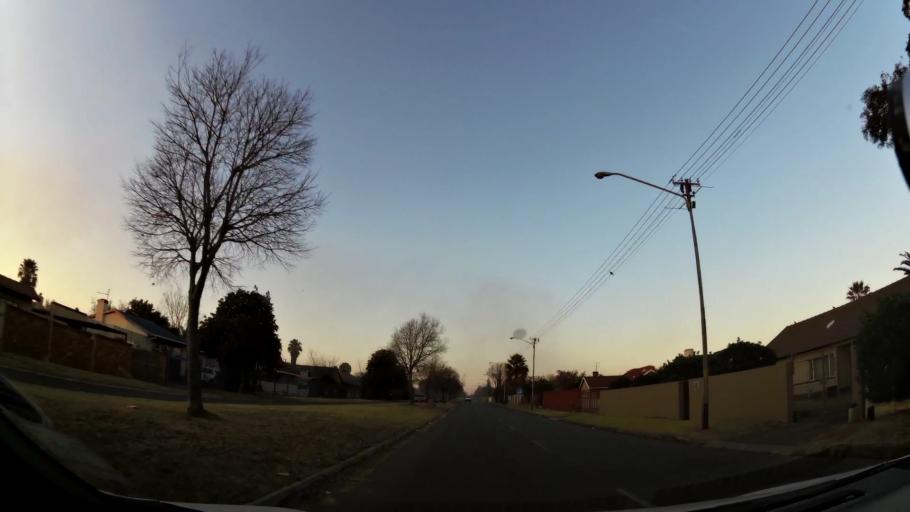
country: ZA
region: Gauteng
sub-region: Ekurhuleni Metropolitan Municipality
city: Germiston
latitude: -26.2706
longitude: 28.1537
